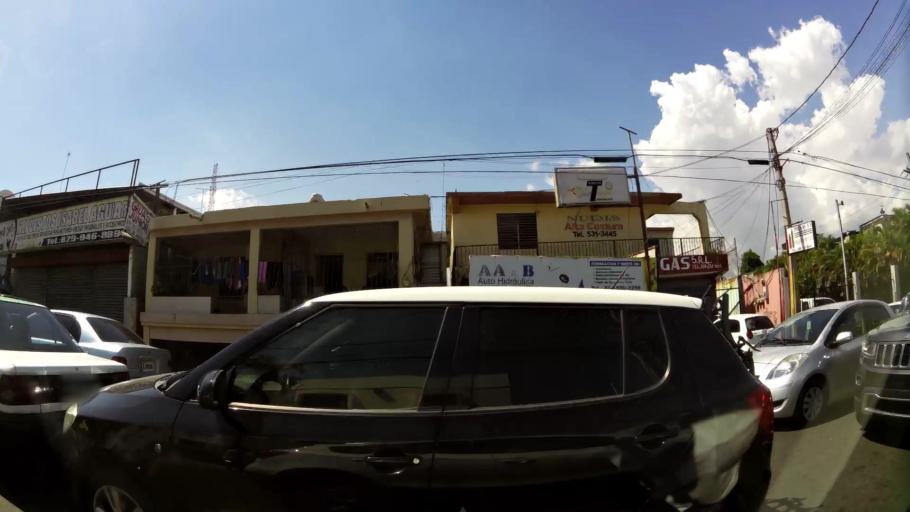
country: DO
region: Nacional
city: Bella Vista
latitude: 18.4523
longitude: -69.9789
